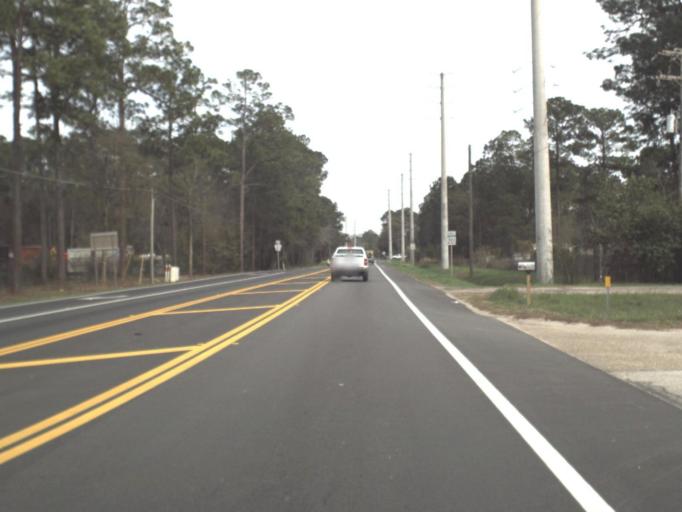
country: US
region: Florida
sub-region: Gadsden County
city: Midway
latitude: 30.4435
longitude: -84.4034
